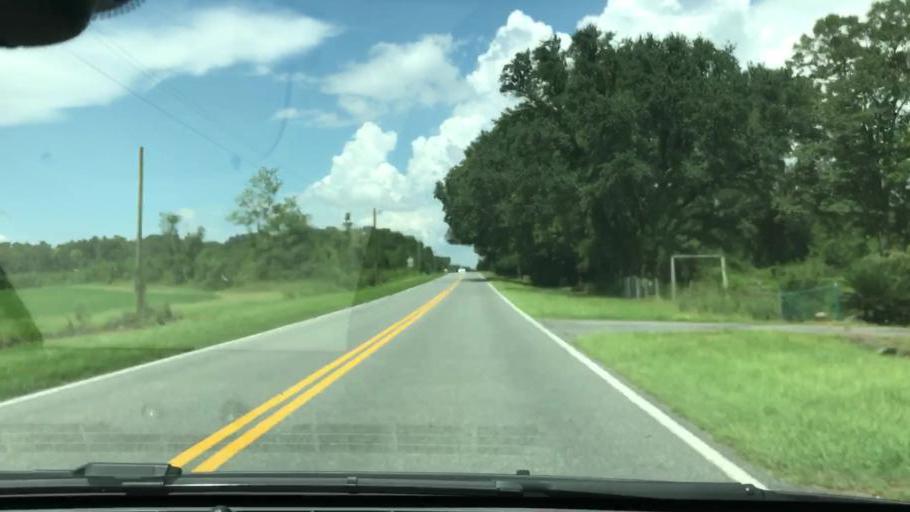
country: US
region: Florida
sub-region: Jackson County
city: Malone
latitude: 30.9493
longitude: -85.1182
